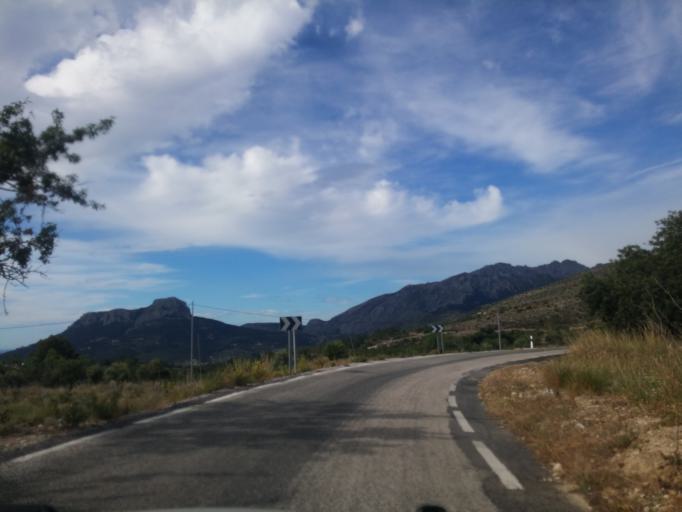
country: ES
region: Valencia
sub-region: Provincia de Alicante
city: Benissa
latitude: 38.7048
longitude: 0.0182
